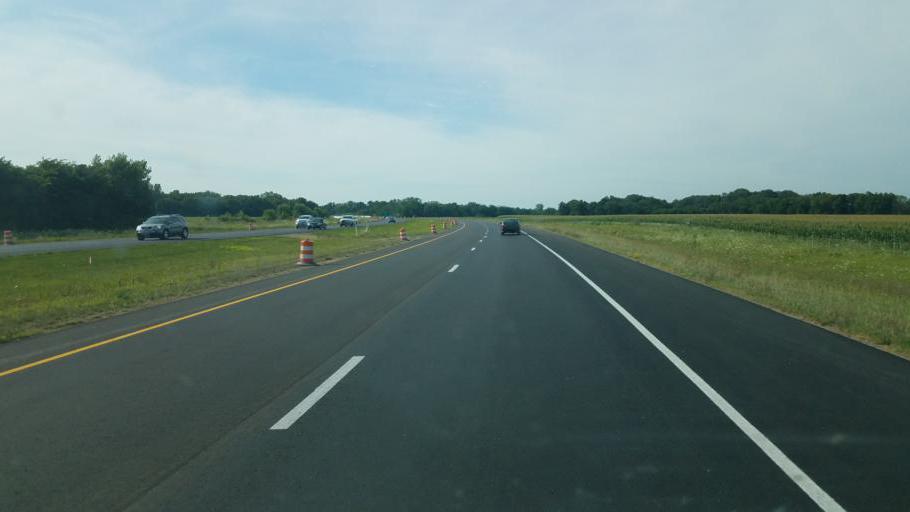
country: US
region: Ohio
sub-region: Fairfield County
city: Lancaster
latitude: 39.7521
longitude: -82.6772
